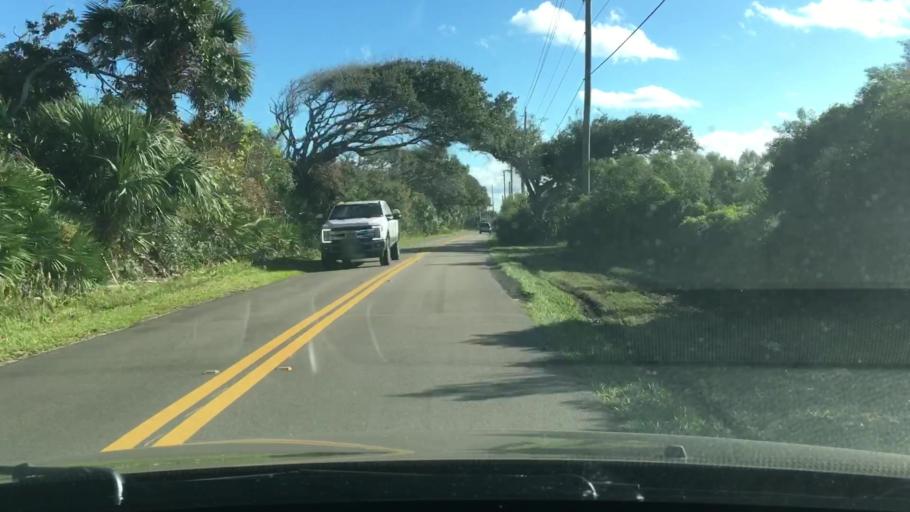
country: US
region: Florida
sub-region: Volusia County
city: Ormond-by-the-Sea
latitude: 29.4046
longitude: -81.0961
